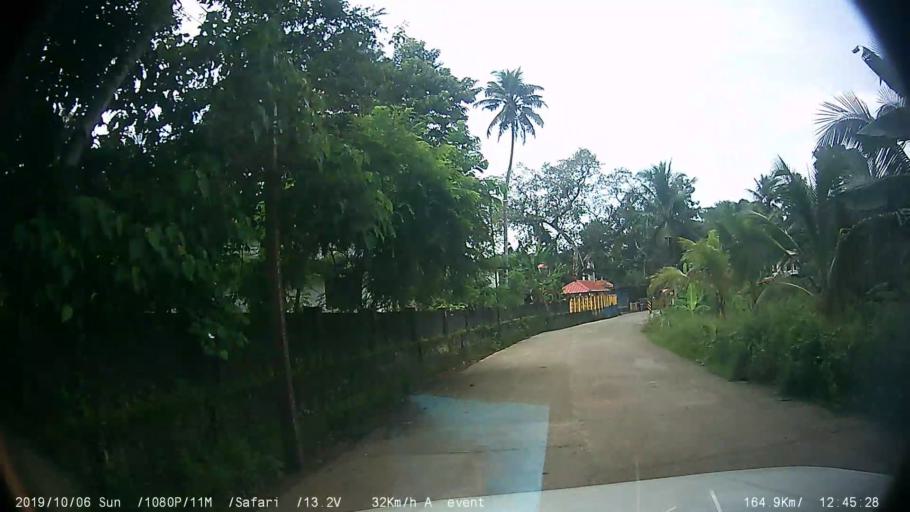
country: IN
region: Kerala
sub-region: Kottayam
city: Palackattumala
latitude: 9.7713
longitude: 76.6118
